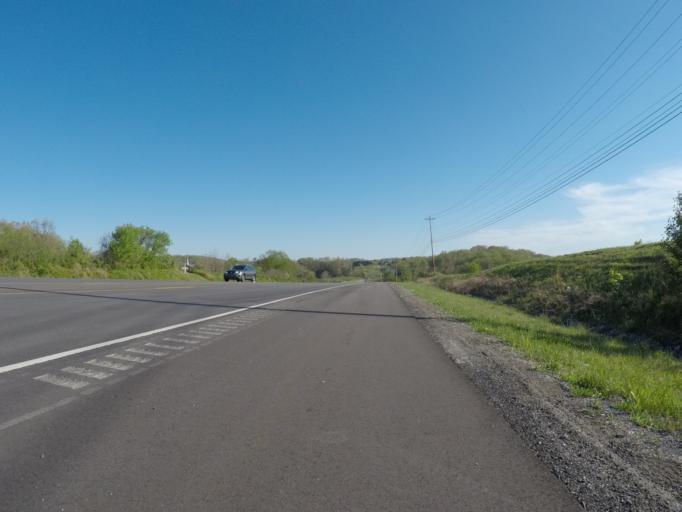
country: US
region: Kentucky
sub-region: Boyd County
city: Meads
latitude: 38.3618
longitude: -82.6980
